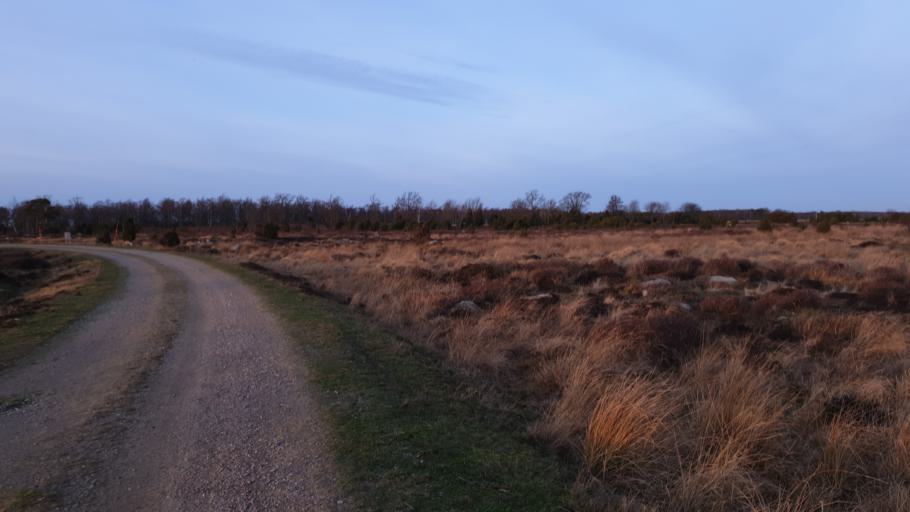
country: SE
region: Blekinge
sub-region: Karlskrona Kommun
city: Jaemjoe
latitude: 56.0789
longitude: 15.8465
